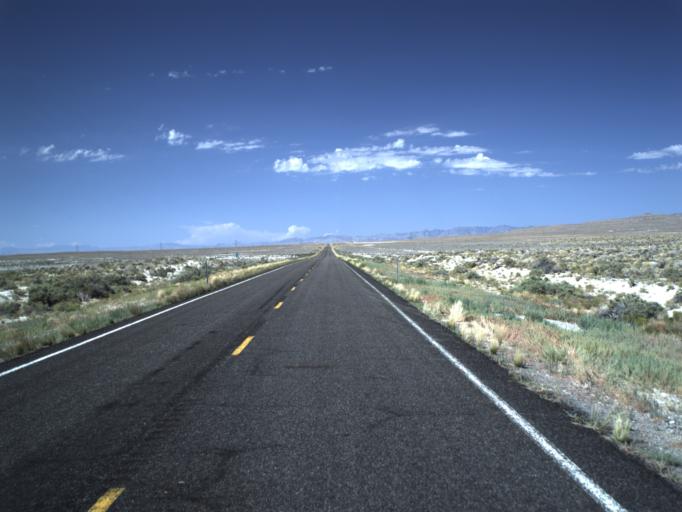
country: US
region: Utah
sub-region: Millard County
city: Delta
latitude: 39.1890
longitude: -113.0028
